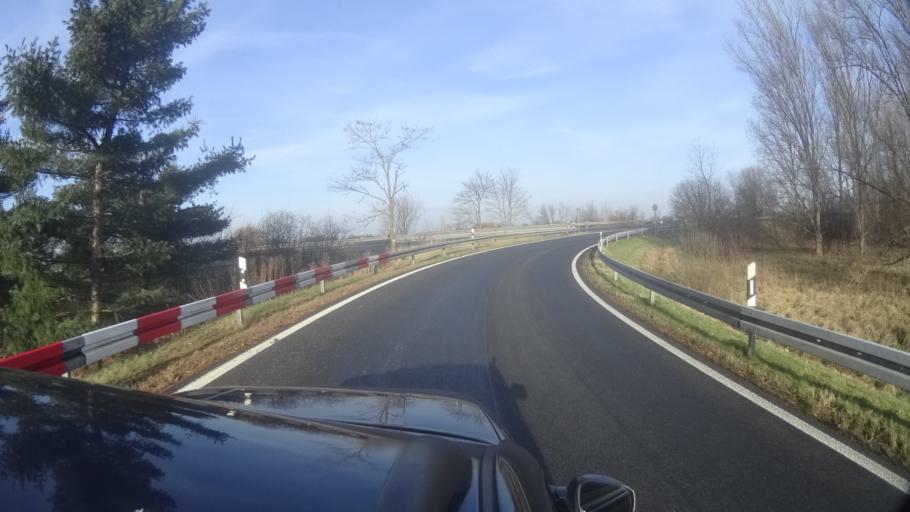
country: DE
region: Brandenburg
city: Velten
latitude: 52.7076
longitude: 13.1021
